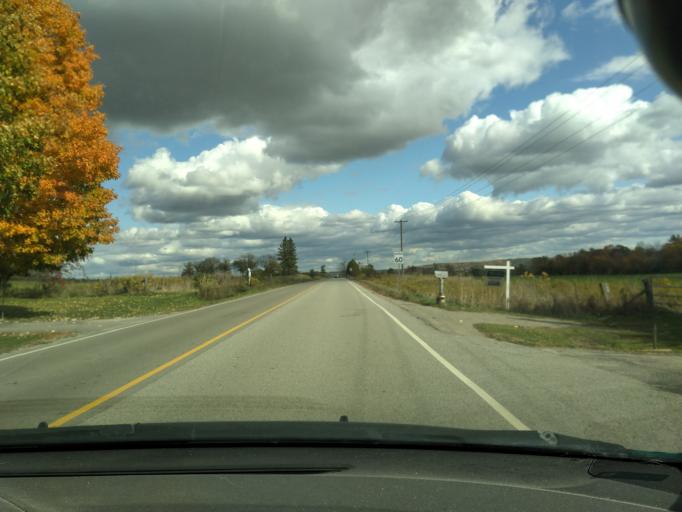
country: CA
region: Ontario
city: Bradford West Gwillimbury
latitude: 44.0833
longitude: -79.5879
